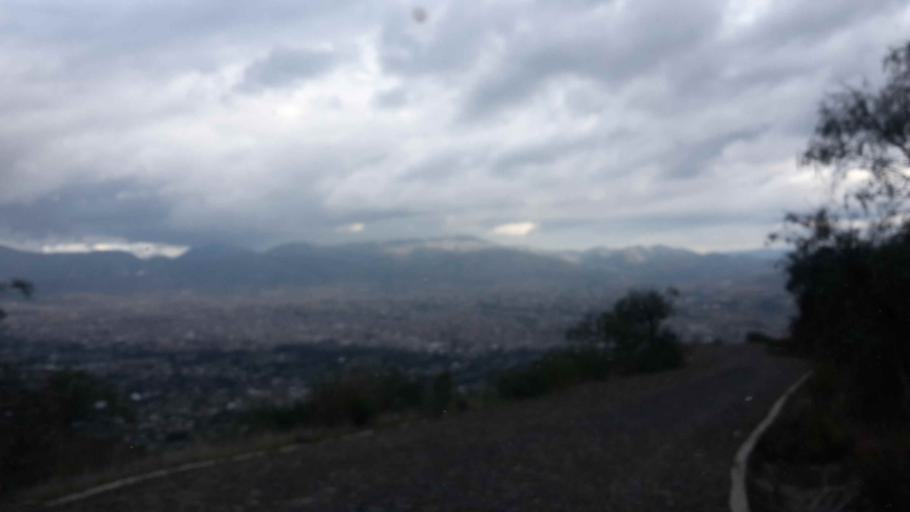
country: BO
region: Cochabamba
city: Cochabamba
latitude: -17.3655
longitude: -66.0629
